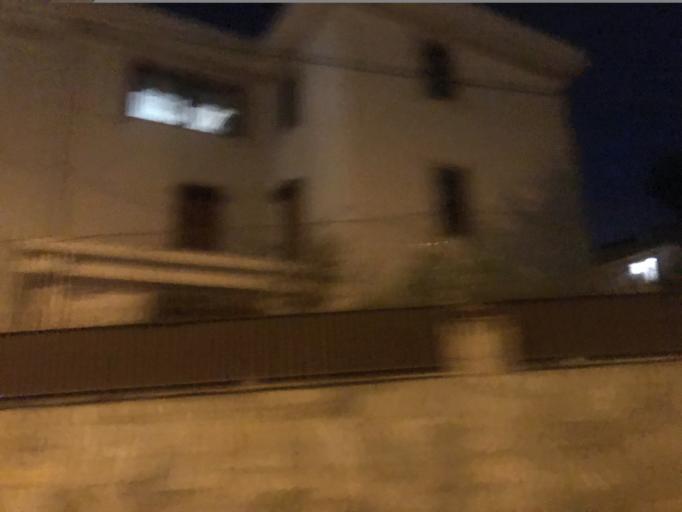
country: TR
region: Istanbul
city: Umraniye
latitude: 41.0331
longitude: 29.1547
